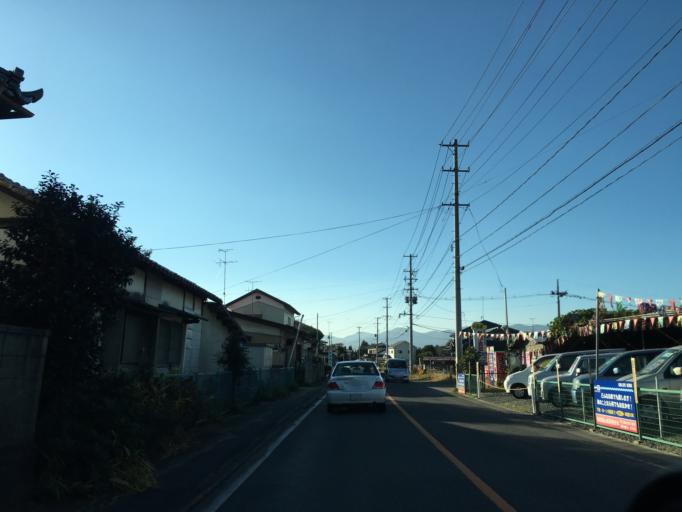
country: JP
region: Fukushima
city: Koriyama
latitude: 37.3896
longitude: 140.3008
